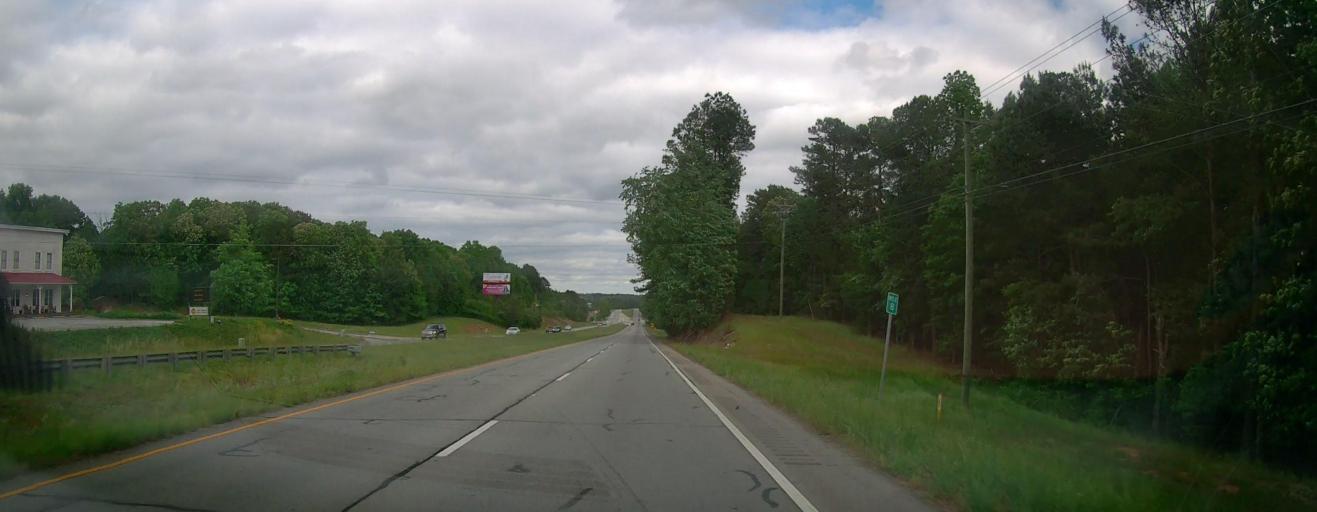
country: US
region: Georgia
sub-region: Walton County
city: Monroe
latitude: 33.8056
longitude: -83.7832
